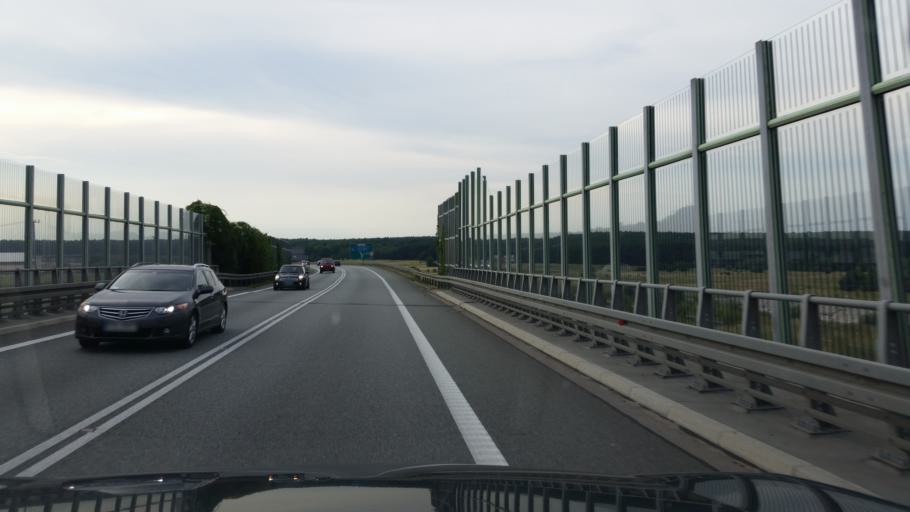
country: PL
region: Silesian Voivodeship
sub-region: Powiat bedzinski
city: Mierzecice
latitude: 50.4469
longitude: 19.1379
